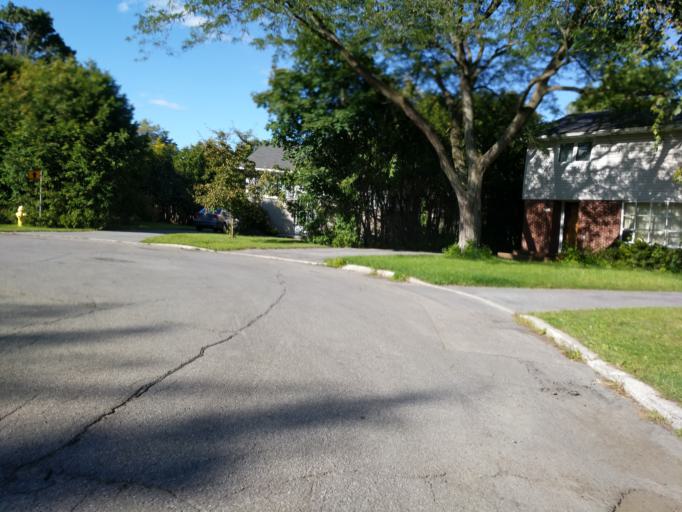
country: CA
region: Ontario
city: Ottawa
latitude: 45.3628
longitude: -75.7452
